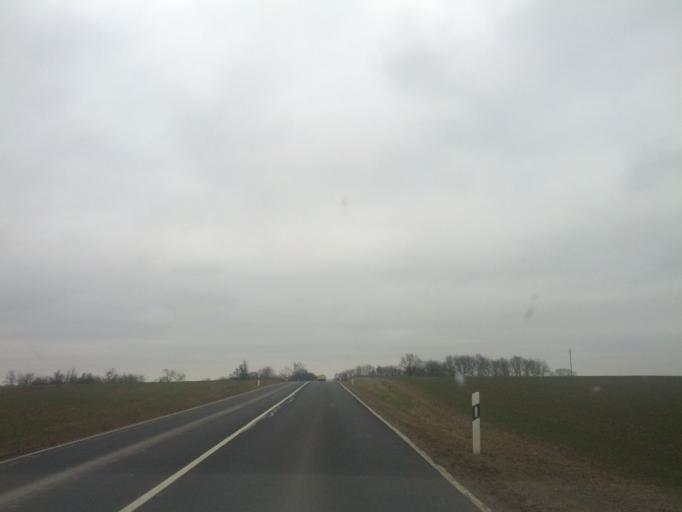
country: DE
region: Thuringia
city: Oberdorla
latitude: 51.1572
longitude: 10.4308
